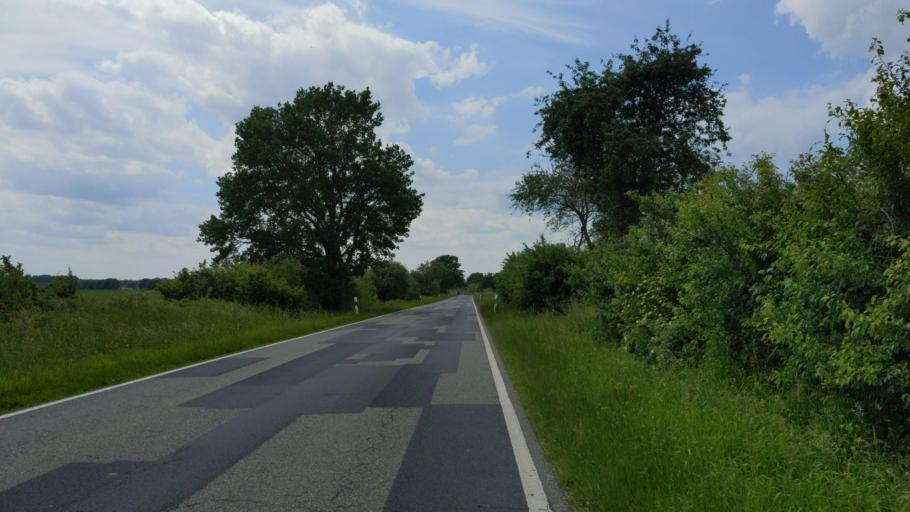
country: DE
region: Mecklenburg-Vorpommern
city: Selmsdorf
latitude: 53.8466
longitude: 10.8029
